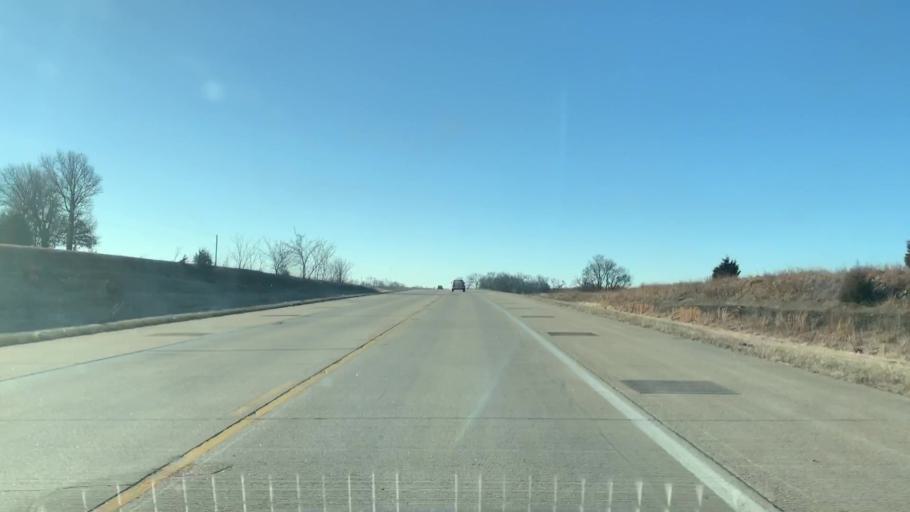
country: US
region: Kansas
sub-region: Crawford County
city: Arma
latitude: 37.5792
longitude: -94.7057
